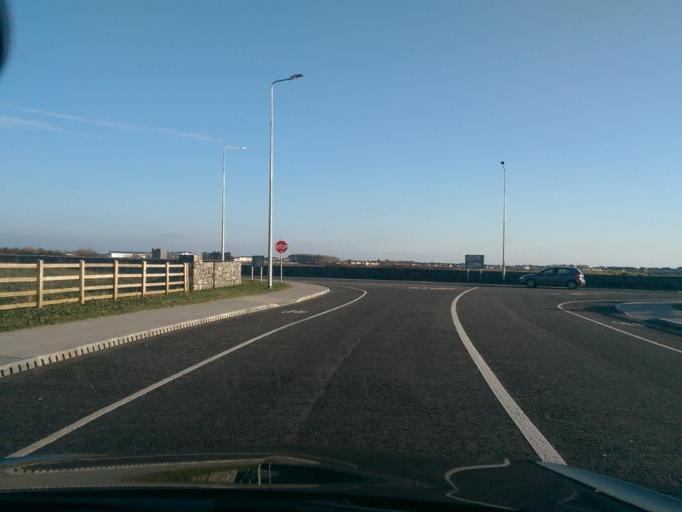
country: IE
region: Connaught
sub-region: County Galway
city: Oranmore
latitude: 53.2742
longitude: -8.9446
